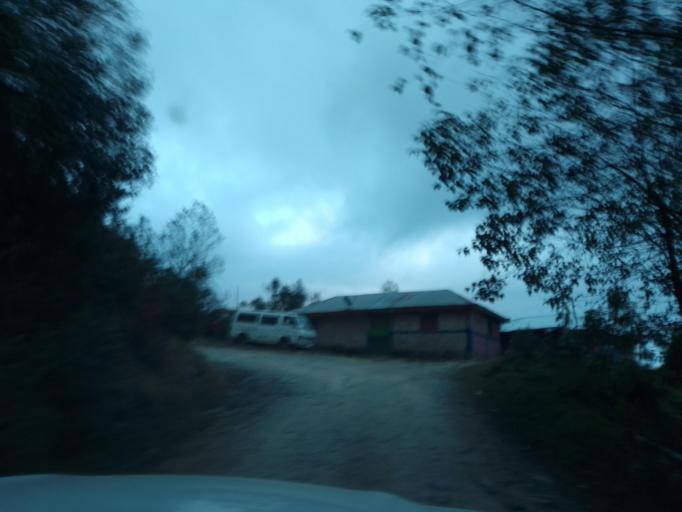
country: MX
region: Chiapas
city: Motozintla de Mendoza
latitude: 15.2189
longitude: -92.2385
